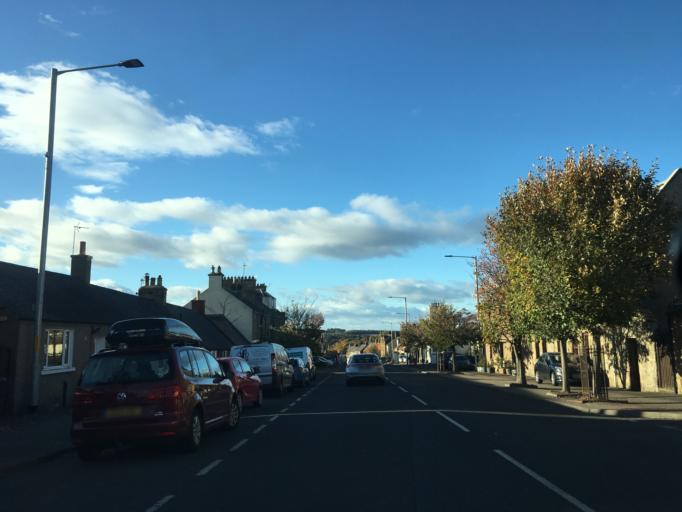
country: GB
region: Scotland
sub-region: Fife
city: Pathhead
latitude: 55.8657
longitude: -2.9652
